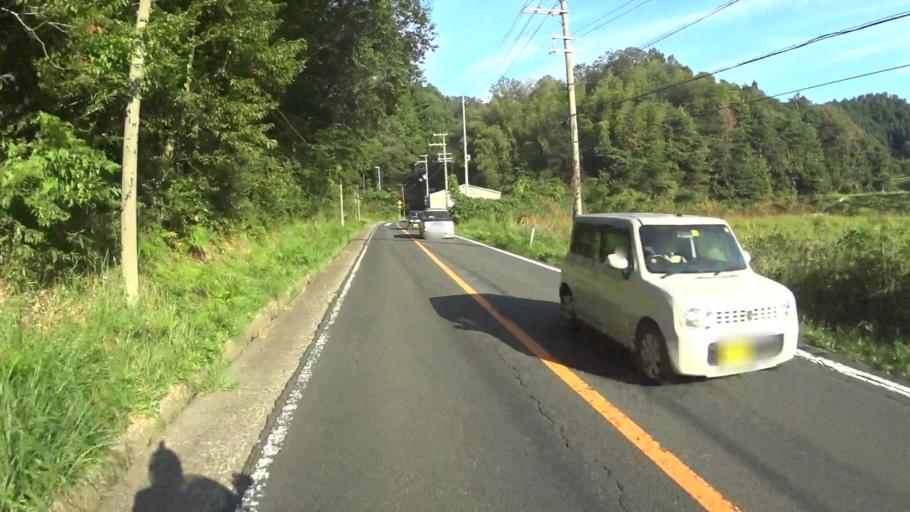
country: JP
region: Hyogo
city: Toyooka
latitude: 35.5943
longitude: 134.9113
